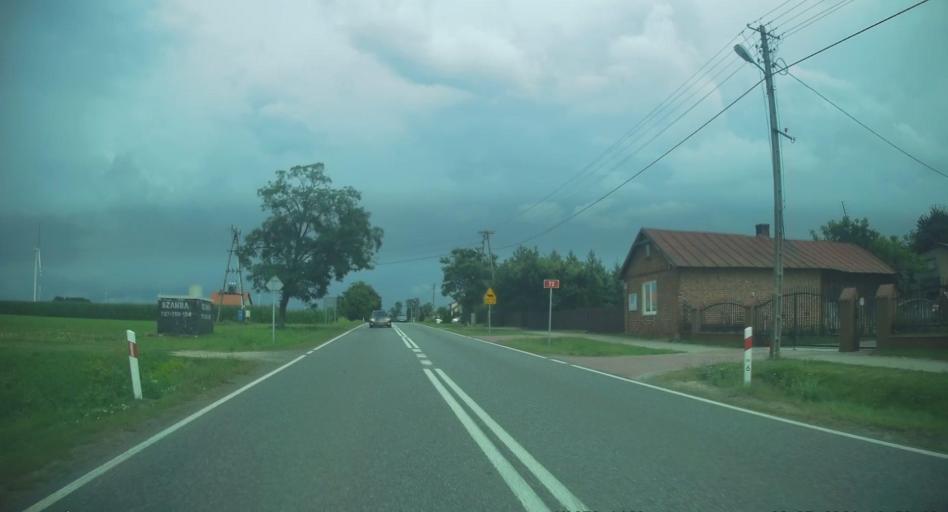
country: PL
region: Lodz Voivodeship
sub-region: Powiat skierniewicki
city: Gluchow
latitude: 51.7719
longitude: 20.1576
